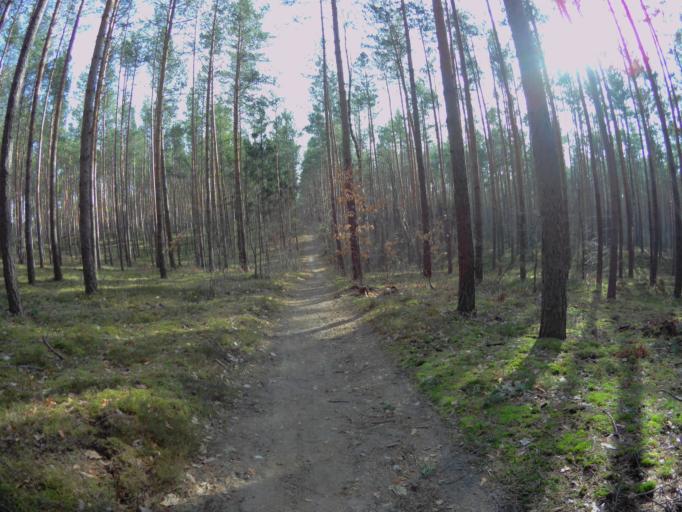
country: PL
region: Subcarpathian Voivodeship
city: Nowa Sarzyna
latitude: 50.3104
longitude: 22.3528
